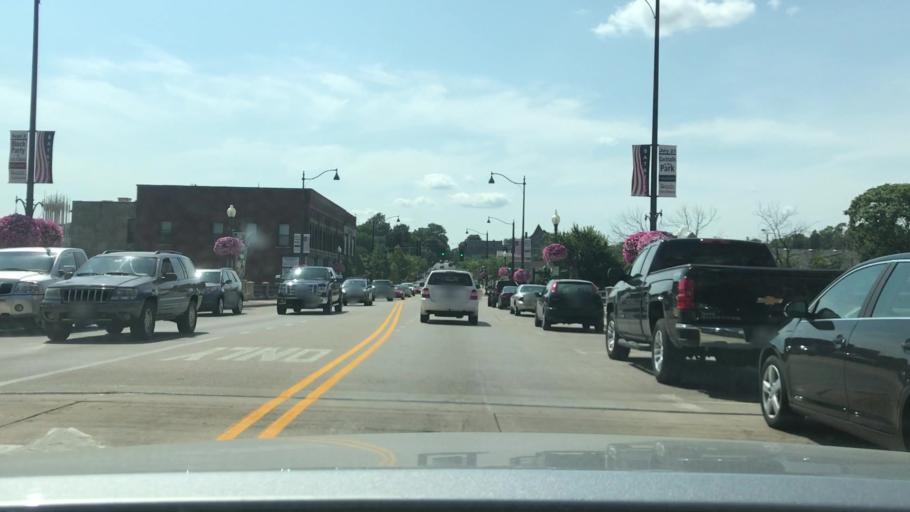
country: US
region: Illinois
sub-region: Kane County
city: Batavia
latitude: 41.8500
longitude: -88.3065
